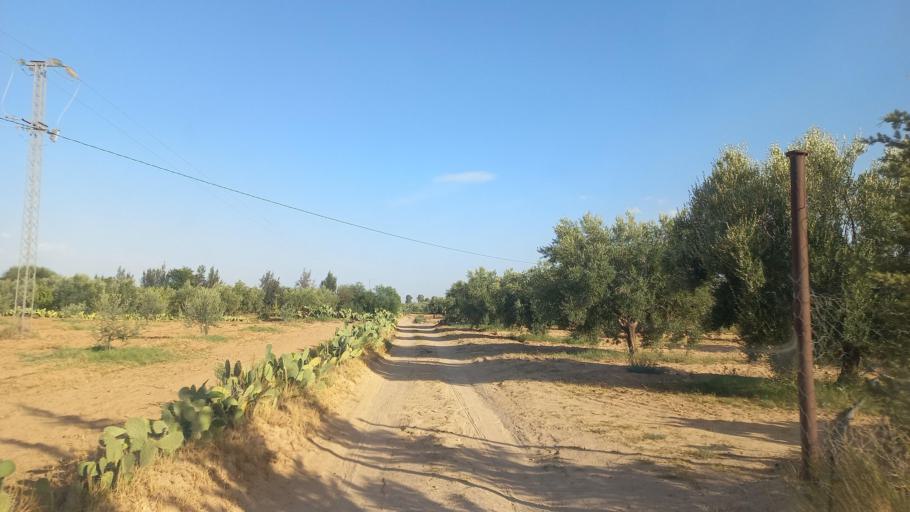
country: TN
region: Al Qasrayn
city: Kasserine
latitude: 35.2640
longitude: 9.0247
